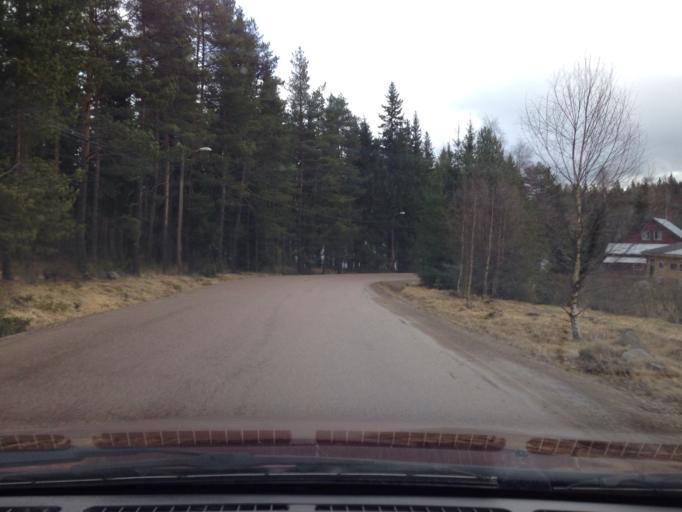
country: SE
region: Dalarna
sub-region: Ludvika Kommun
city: Ludvika
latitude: 60.1771
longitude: 15.2886
